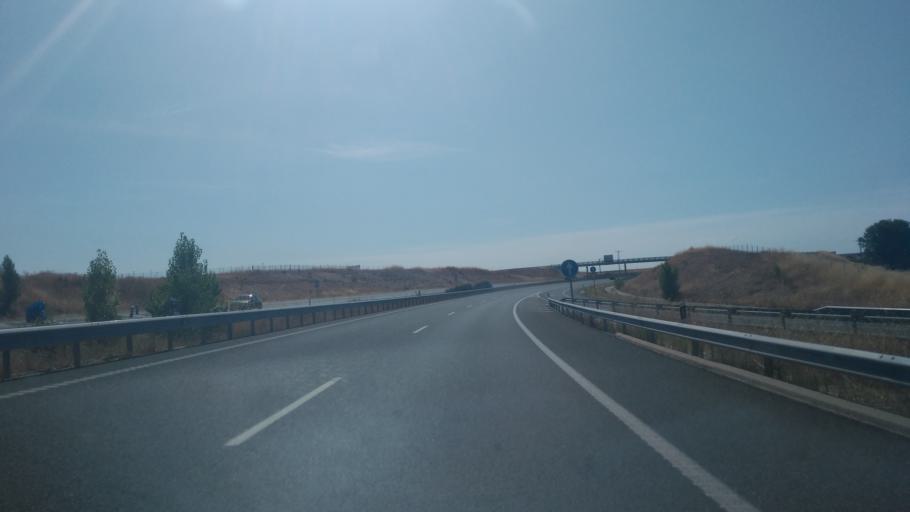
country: ES
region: Castille and Leon
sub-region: Provincia de Salamanca
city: Pelabravo
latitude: 40.9431
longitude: -5.5977
